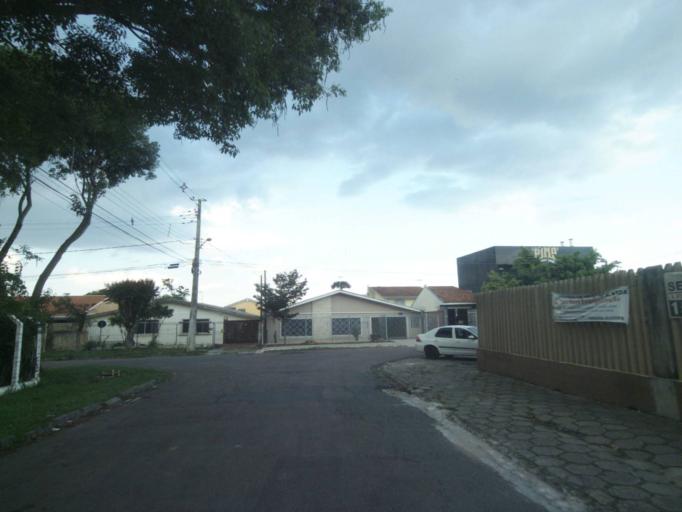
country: BR
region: Parana
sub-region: Sao Jose Dos Pinhais
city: Sao Jose dos Pinhais
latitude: -25.5343
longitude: -49.2728
